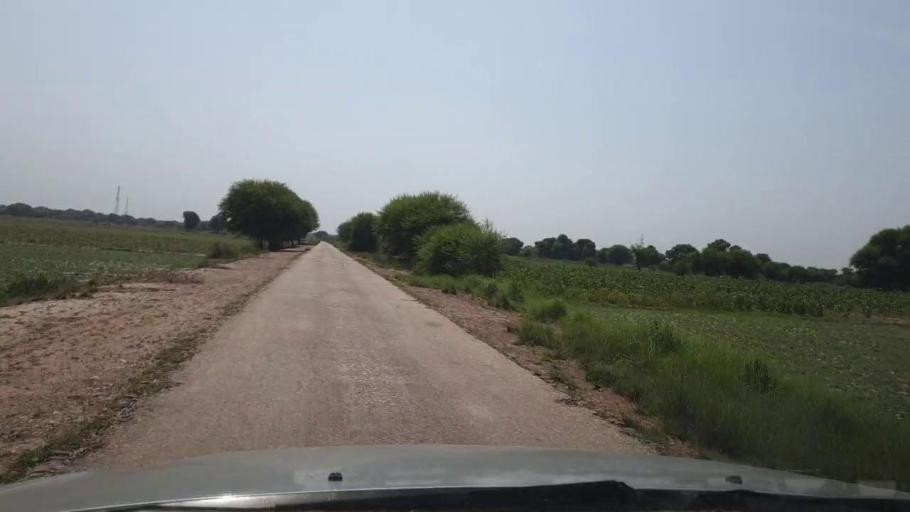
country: PK
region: Sindh
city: Chambar
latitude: 25.2271
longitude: 68.7776
